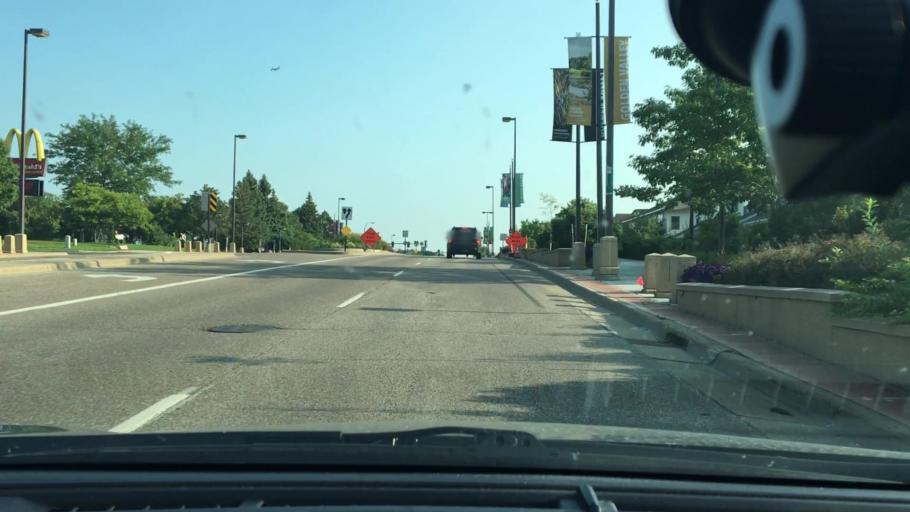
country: US
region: Minnesota
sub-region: Hennepin County
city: Golden Valley
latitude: 44.9875
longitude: -93.3805
